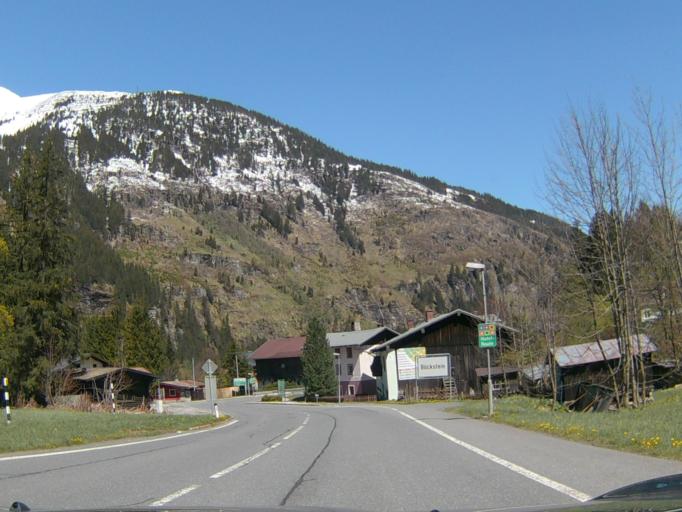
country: AT
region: Salzburg
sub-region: Politischer Bezirk Sankt Johann im Pongau
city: Bad Gastein
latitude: 47.0863
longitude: 13.1203
